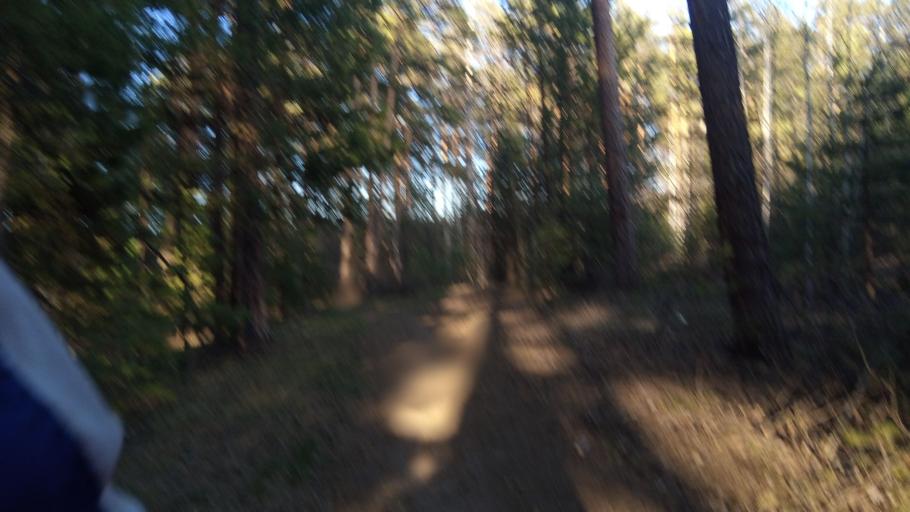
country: RU
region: Chelyabinsk
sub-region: Gorod Chelyabinsk
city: Chelyabinsk
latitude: 55.1385
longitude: 61.3359
